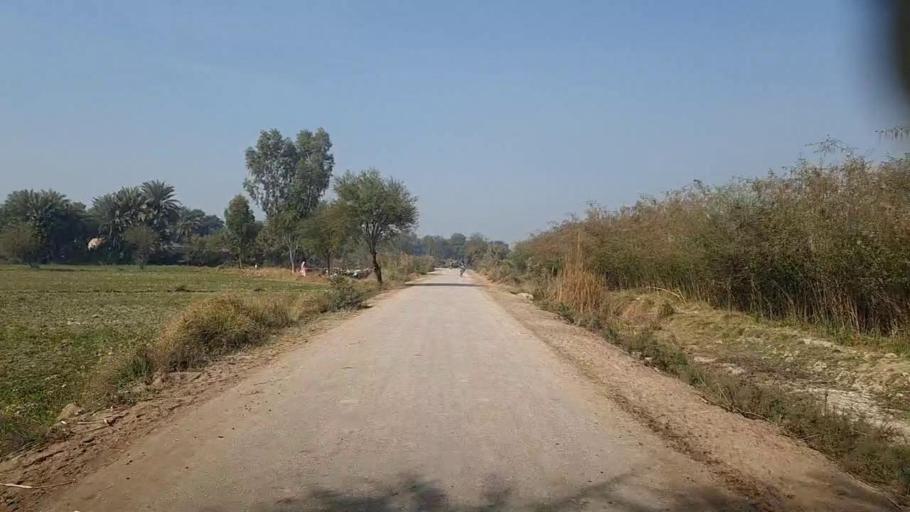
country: PK
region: Sindh
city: Khairpur
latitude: 27.9639
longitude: 69.6671
